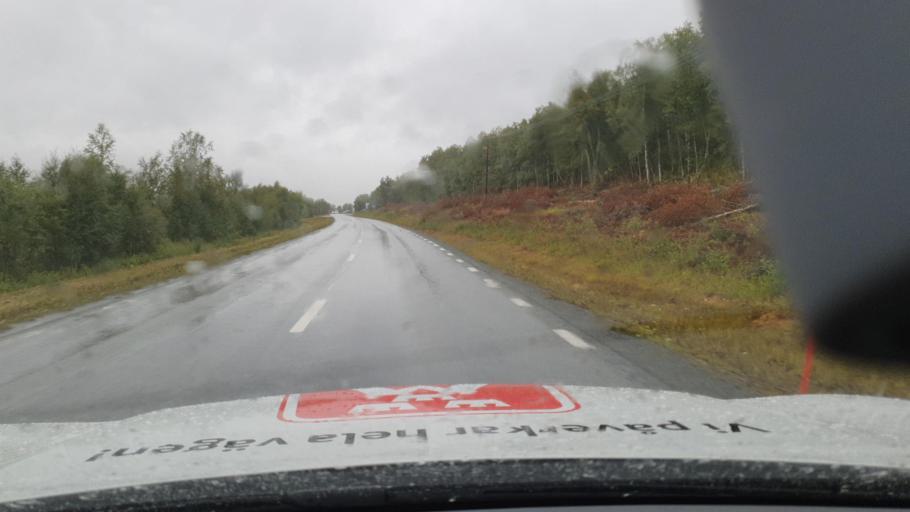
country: NO
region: Nordland
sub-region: Rana
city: Mo i Rana
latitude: 65.8028
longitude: 15.0944
